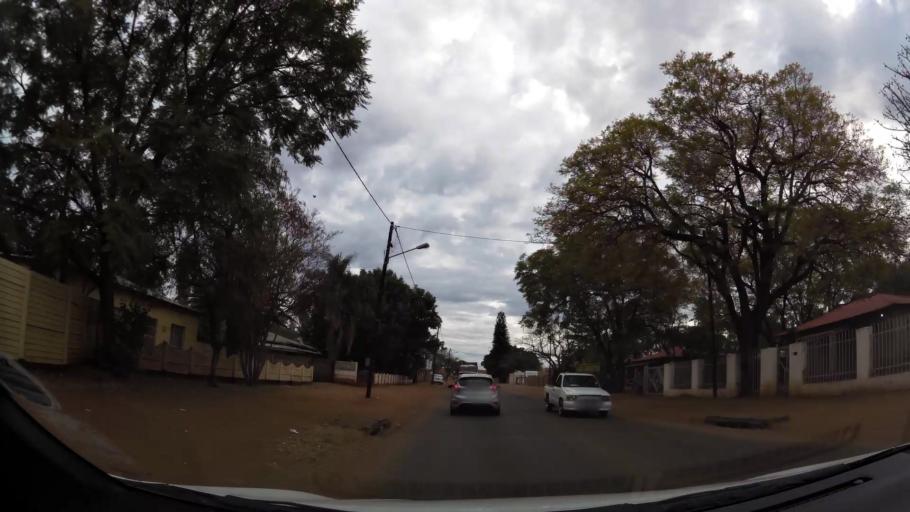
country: ZA
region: Limpopo
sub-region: Waterberg District Municipality
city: Modimolle
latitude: -24.5222
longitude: 28.7093
